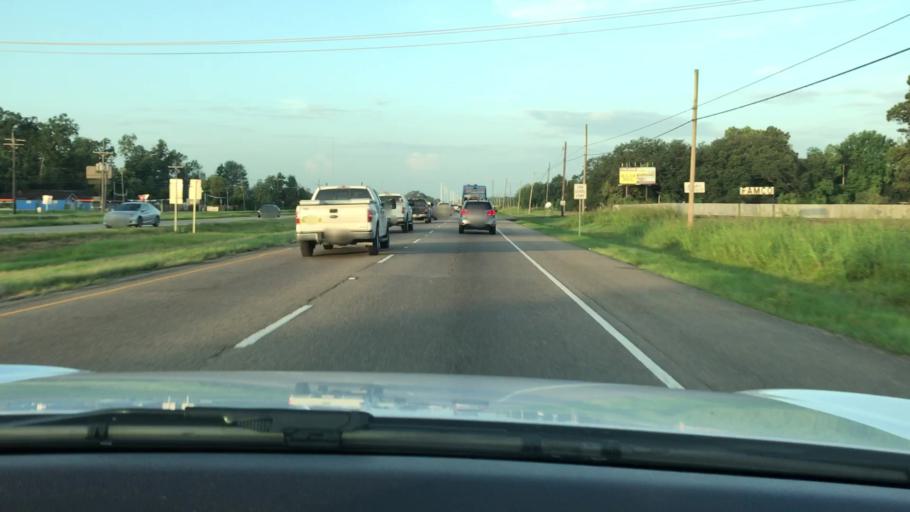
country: US
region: Louisiana
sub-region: West Baton Rouge Parish
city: Brusly
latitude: 30.3803
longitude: -91.2498
